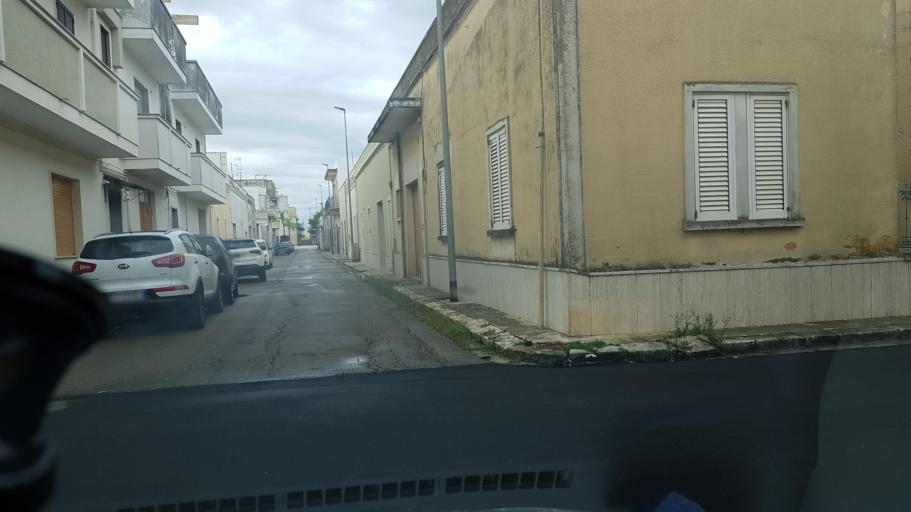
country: IT
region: Apulia
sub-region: Provincia di Lecce
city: Carmiano
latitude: 40.3477
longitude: 18.0407
